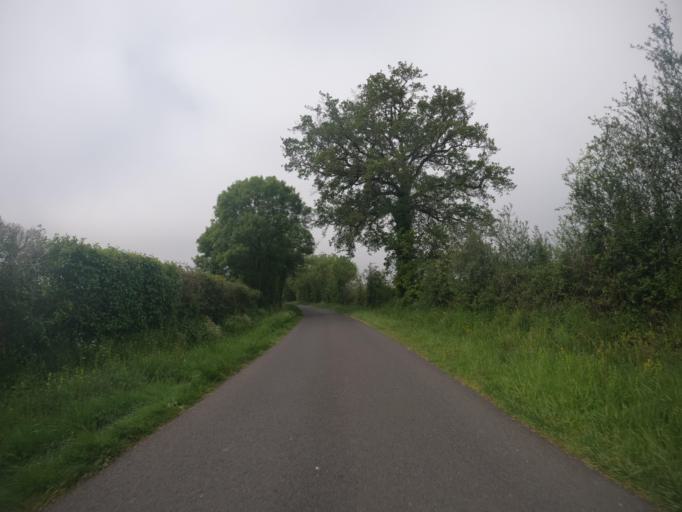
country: FR
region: Poitou-Charentes
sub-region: Departement des Deux-Sevres
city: Chiche
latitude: 46.8739
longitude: -0.3362
